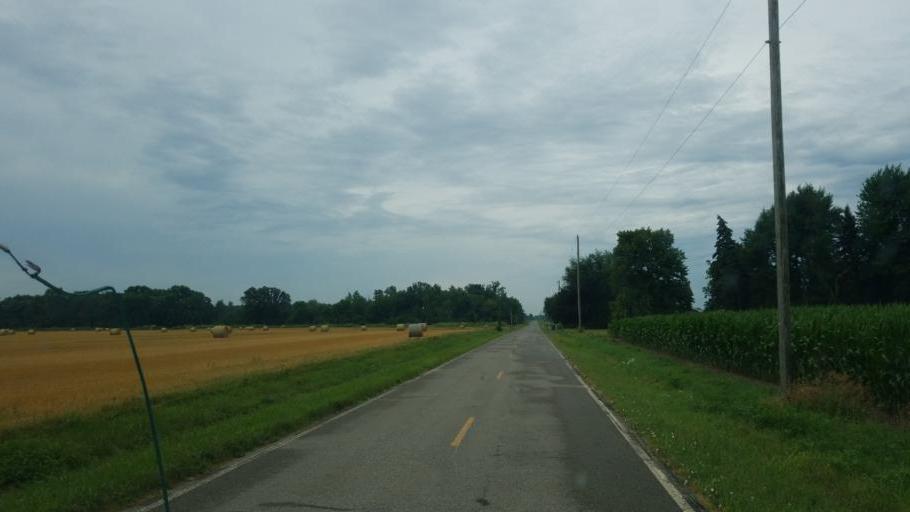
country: US
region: Ohio
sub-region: Defiance County
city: Hicksville
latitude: 41.2635
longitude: -84.6894
